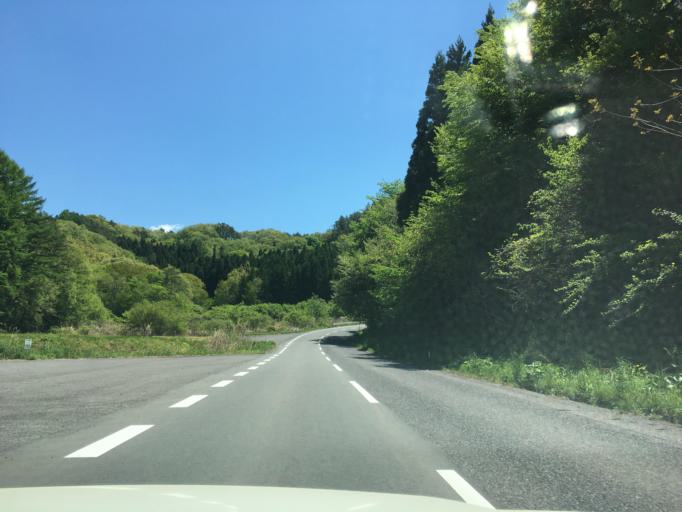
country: JP
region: Fukushima
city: Funehikimachi-funehiki
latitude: 37.3891
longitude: 140.6090
